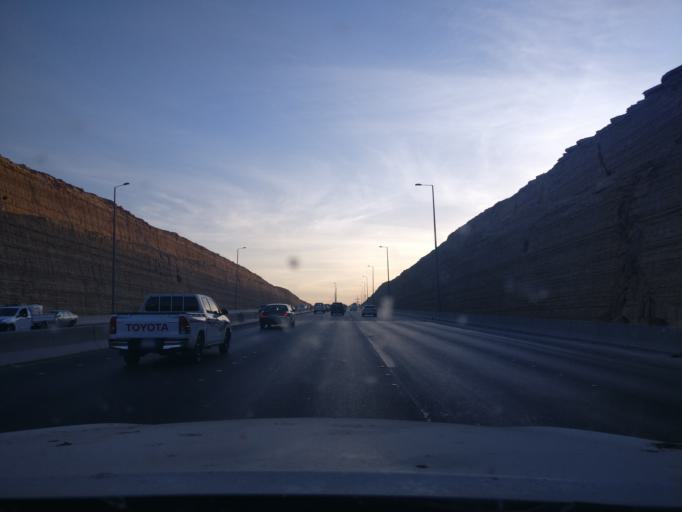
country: SA
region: Ar Riyad
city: Riyadh
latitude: 24.6082
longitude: 46.5610
